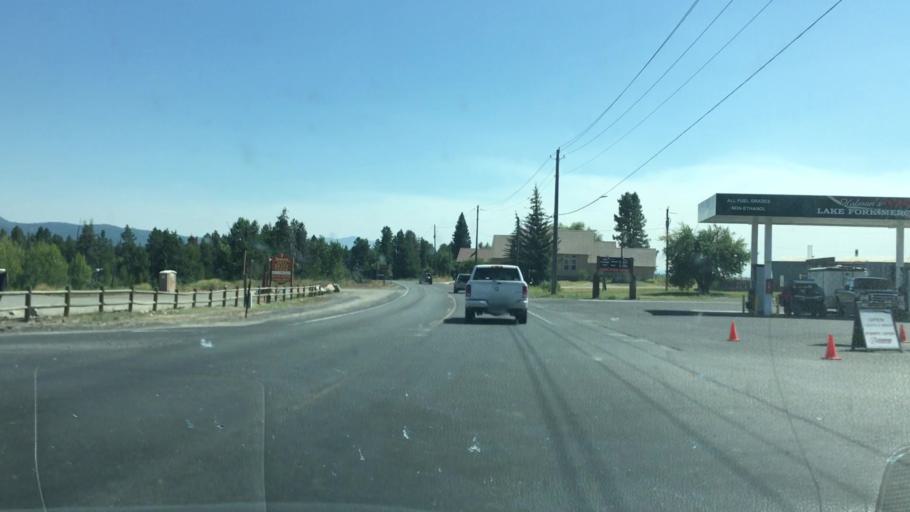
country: US
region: Idaho
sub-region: Valley County
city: McCall
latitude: 44.8327
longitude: -116.0845
